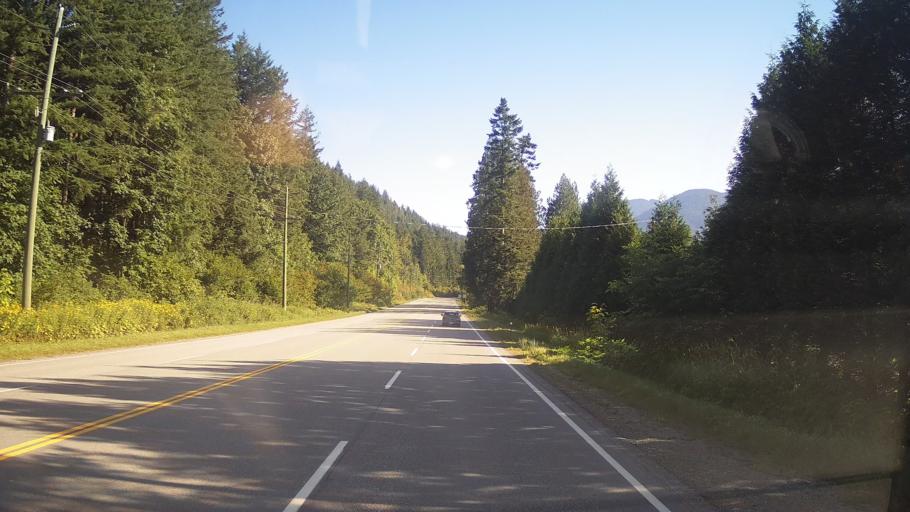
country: CA
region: British Columbia
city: Hope
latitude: 49.4572
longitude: -121.4359
